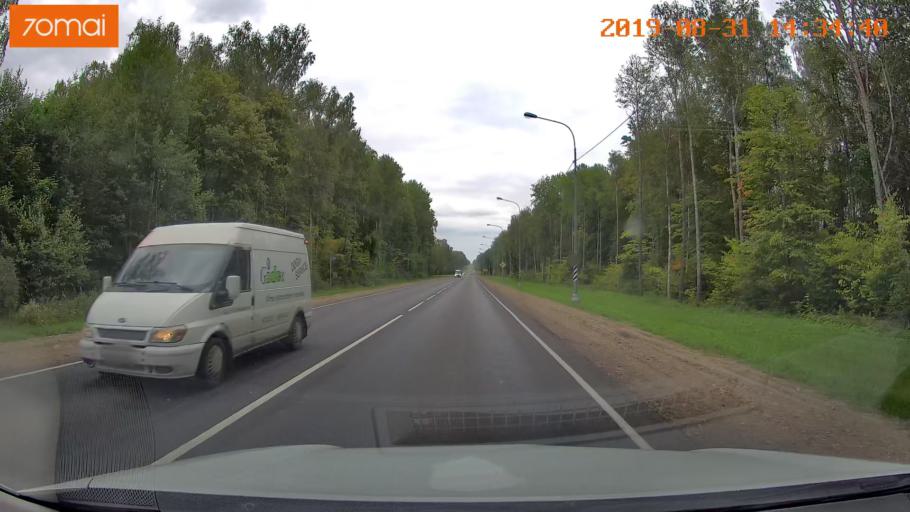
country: RU
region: Smolensk
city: Yekimovichi
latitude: 54.1586
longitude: 33.4417
